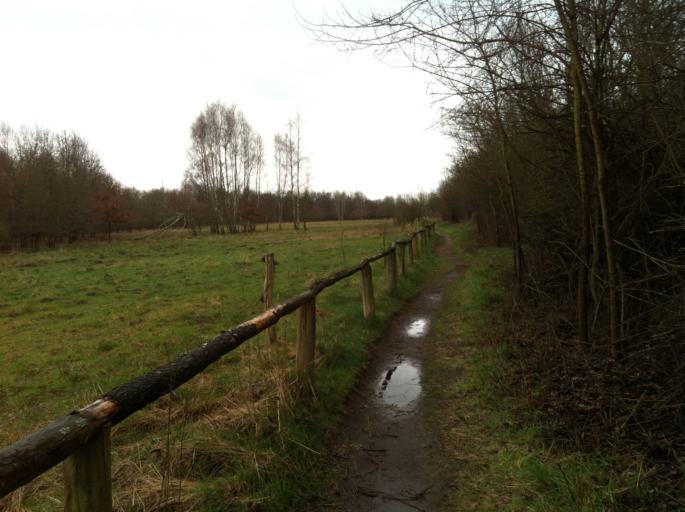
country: DE
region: Berlin
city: Karow
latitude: 52.6273
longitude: 13.4613
